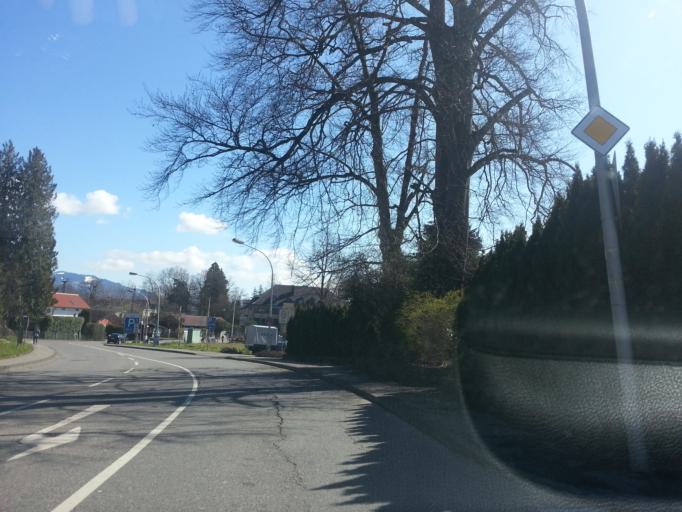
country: DE
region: Bavaria
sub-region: Swabia
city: Lindau
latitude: 47.5530
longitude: 9.6920
